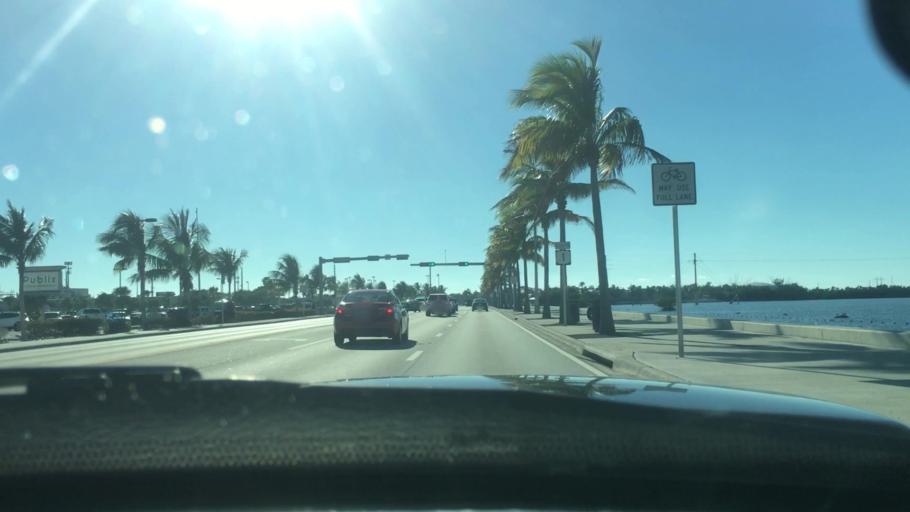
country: US
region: Florida
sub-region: Monroe County
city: Key West
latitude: 24.5711
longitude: -81.7641
